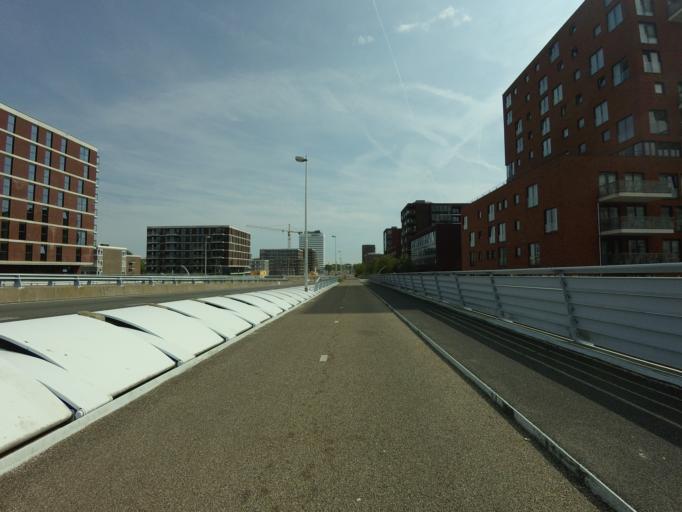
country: NL
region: Utrecht
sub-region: Gemeente Utrecht
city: Utrecht
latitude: 52.0713
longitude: 5.0895
